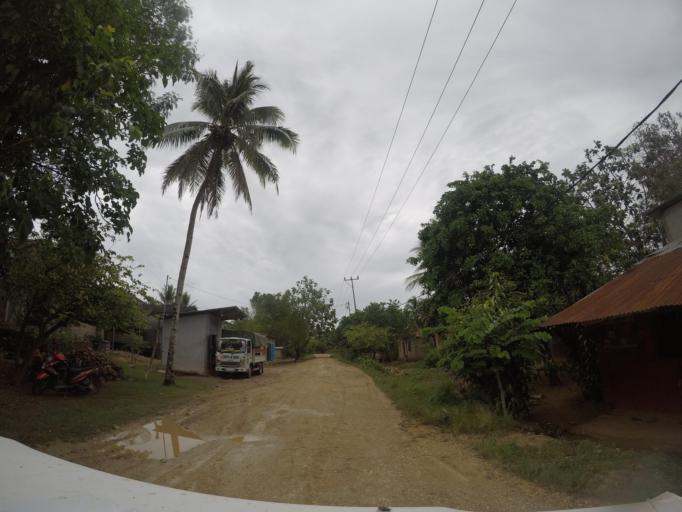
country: TL
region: Lautem
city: Lospalos
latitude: -8.5370
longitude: 126.9967
